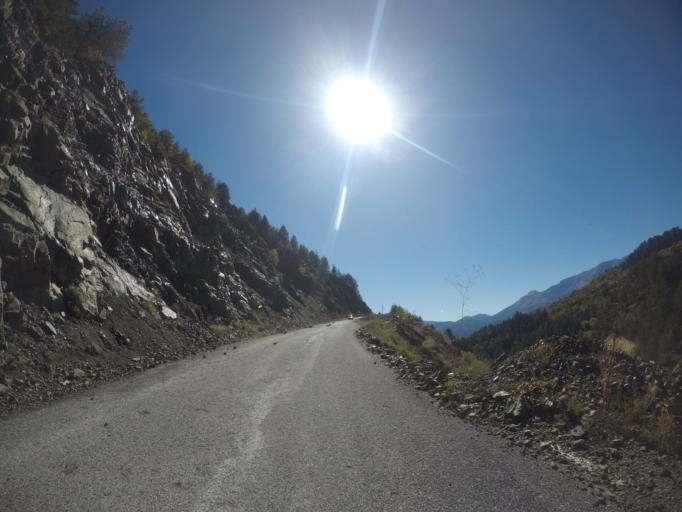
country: GR
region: Epirus
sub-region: Nomos Ioanninon
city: Konitsa
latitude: 40.0415
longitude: 20.9168
